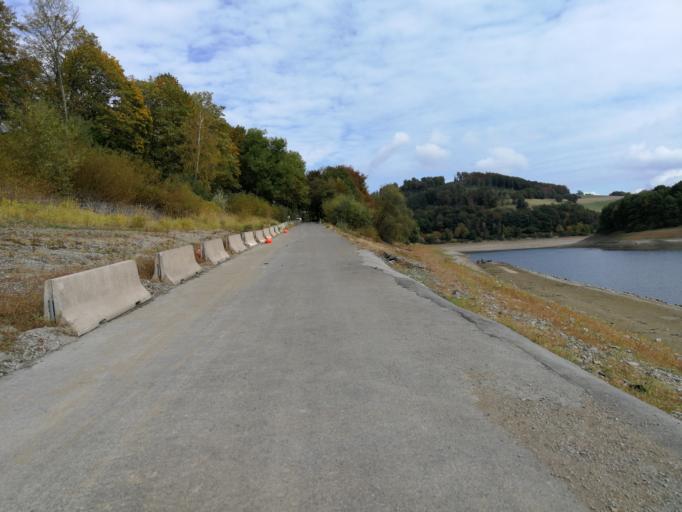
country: DE
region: North Rhine-Westphalia
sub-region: Regierungsbezirk Arnsberg
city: Meschede
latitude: 51.3128
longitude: 8.2627
